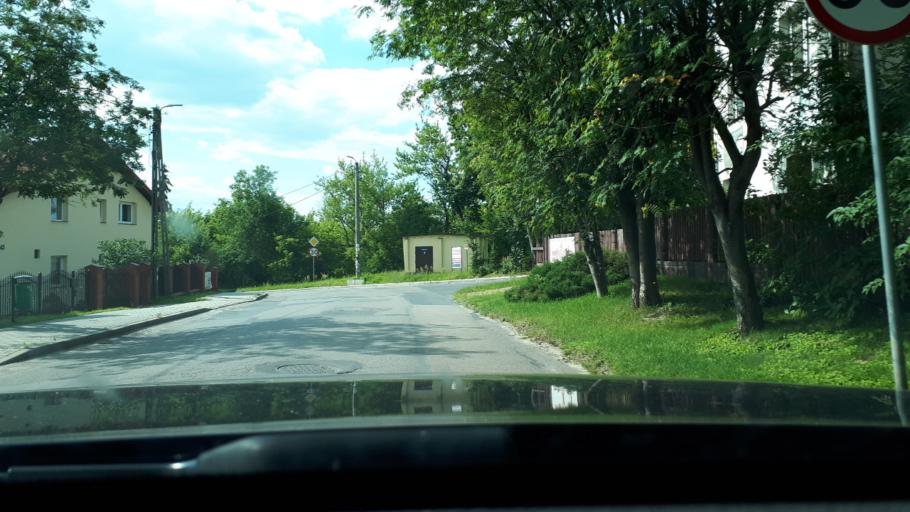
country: PL
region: Masovian Voivodeship
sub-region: Powiat grojecki
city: Warka
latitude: 51.7903
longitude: 21.1942
